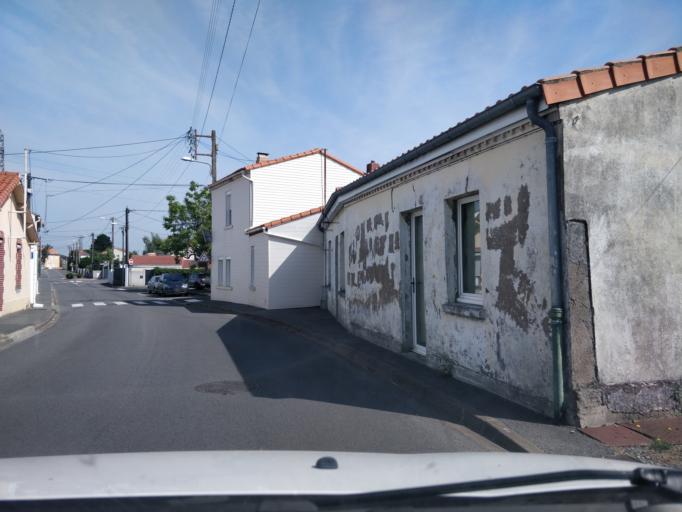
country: FR
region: Pays de la Loire
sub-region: Departement de la Loire-Atlantique
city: Saint-Sebastien-sur-Loire
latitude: 47.2010
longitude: -1.4933
